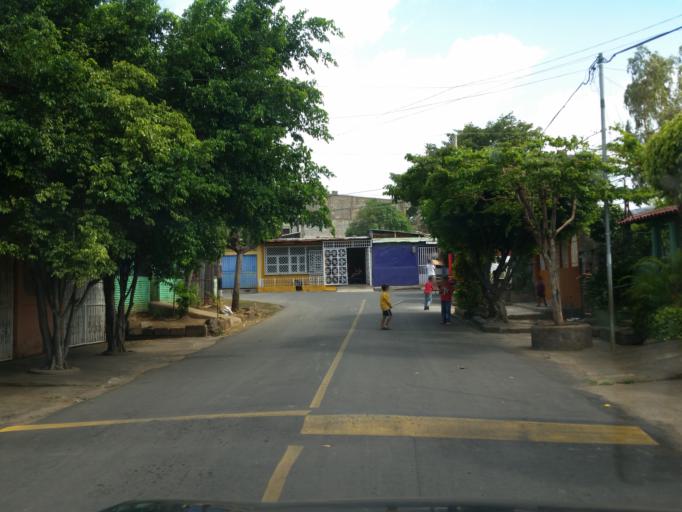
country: NI
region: Managua
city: Managua
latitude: 12.1312
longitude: -86.2537
